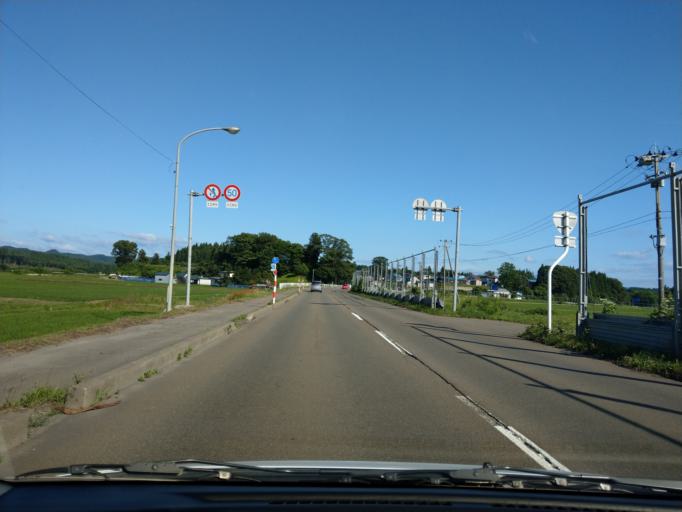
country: JP
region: Akita
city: Takanosu
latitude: 40.1938
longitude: 140.3986
